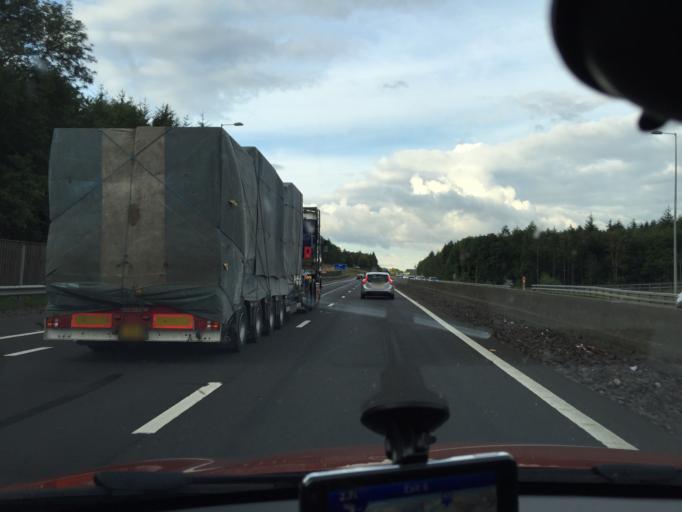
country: GB
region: Scotland
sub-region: North Lanarkshire
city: Cumbernauld
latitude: 55.9476
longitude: -4.0065
